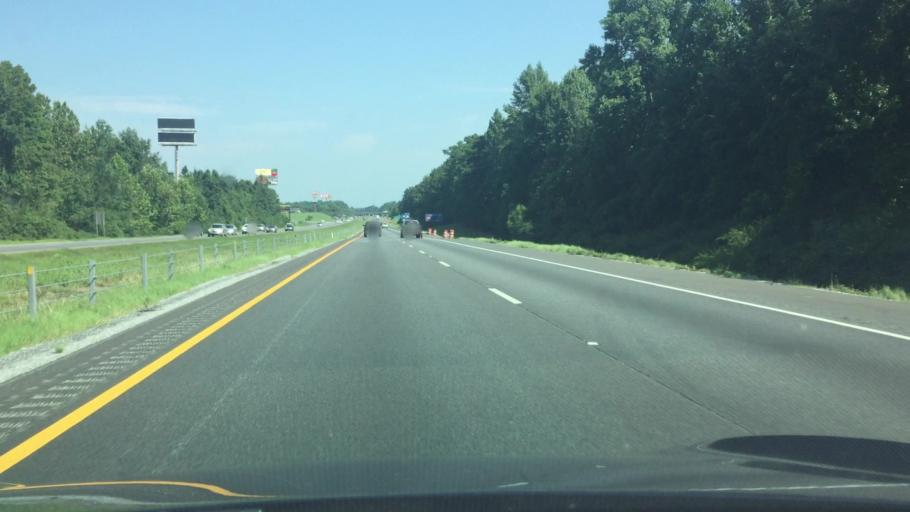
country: US
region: Alabama
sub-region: Chilton County
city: Clanton
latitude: 32.8353
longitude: -86.5922
